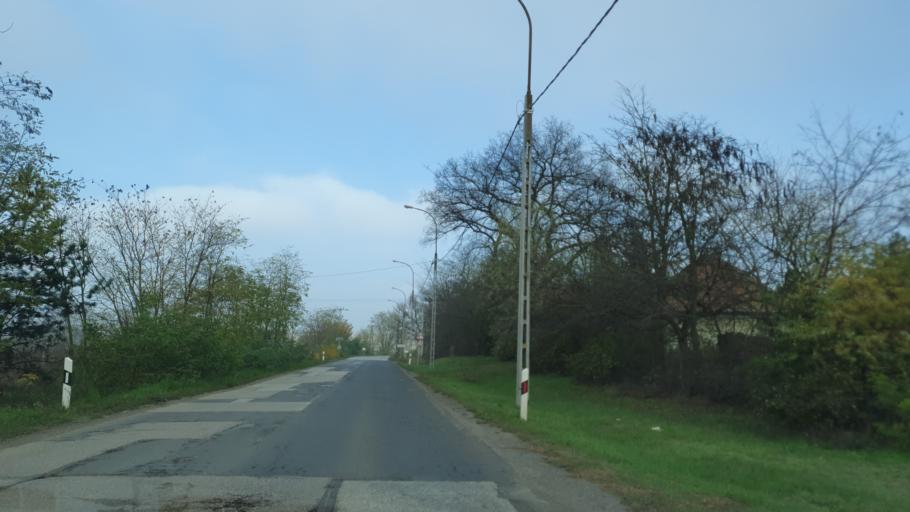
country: HU
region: Pest
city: Orbottyan
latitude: 47.6773
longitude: 19.2552
